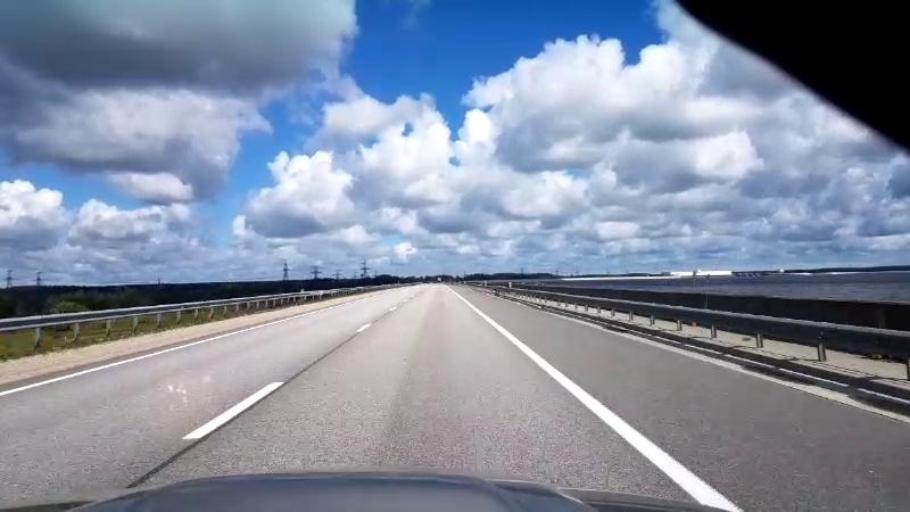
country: LV
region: Kekava
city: Kekava
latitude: 56.8359
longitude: 24.2690
